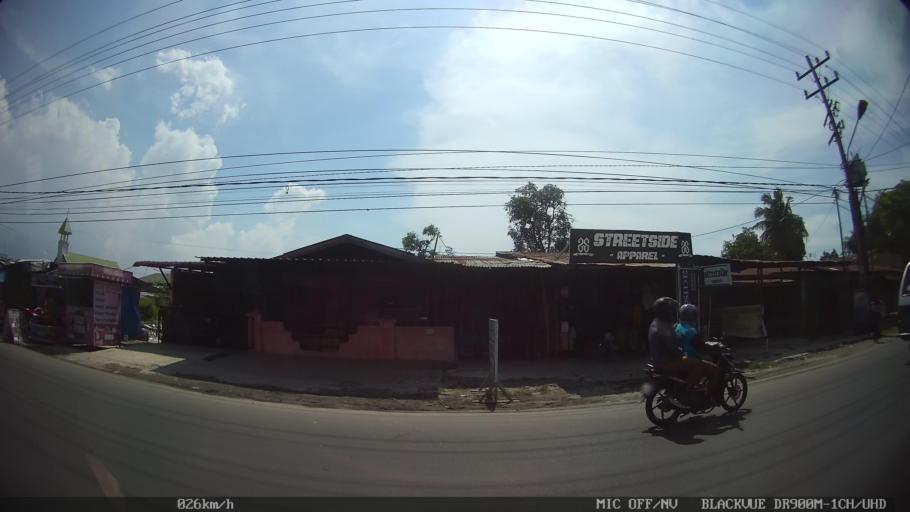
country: ID
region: North Sumatra
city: Medan
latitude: 3.6349
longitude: 98.6595
